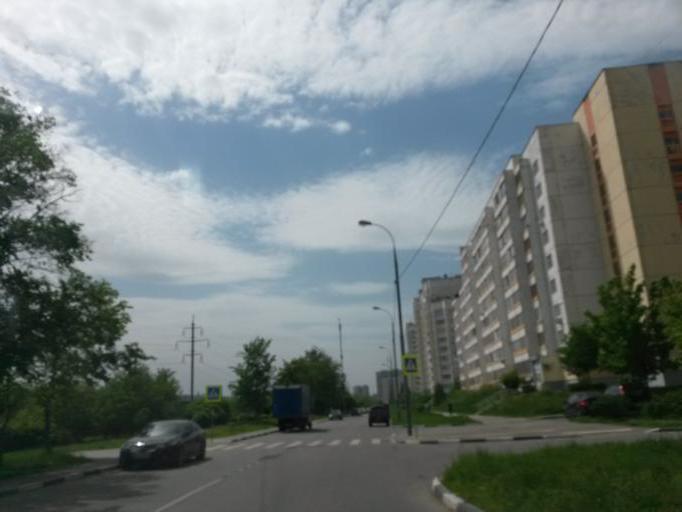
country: RU
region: Moskovskaya
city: Kommunarka
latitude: 55.5416
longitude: 37.5272
